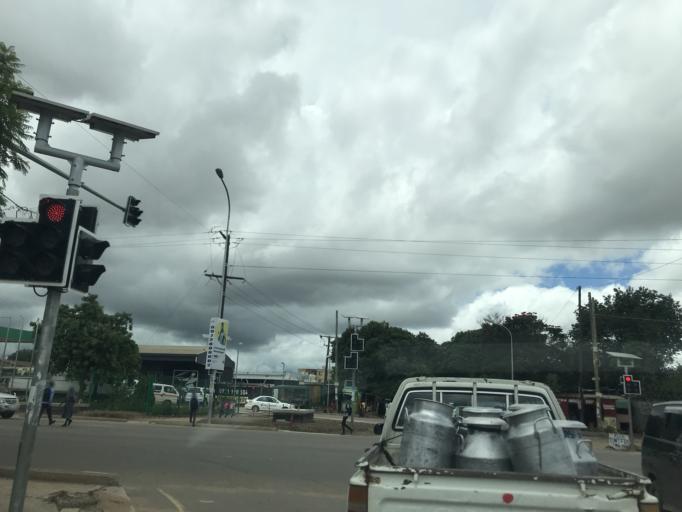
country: ZM
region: Lusaka
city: Lusaka
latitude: -15.4297
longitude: 28.3027
